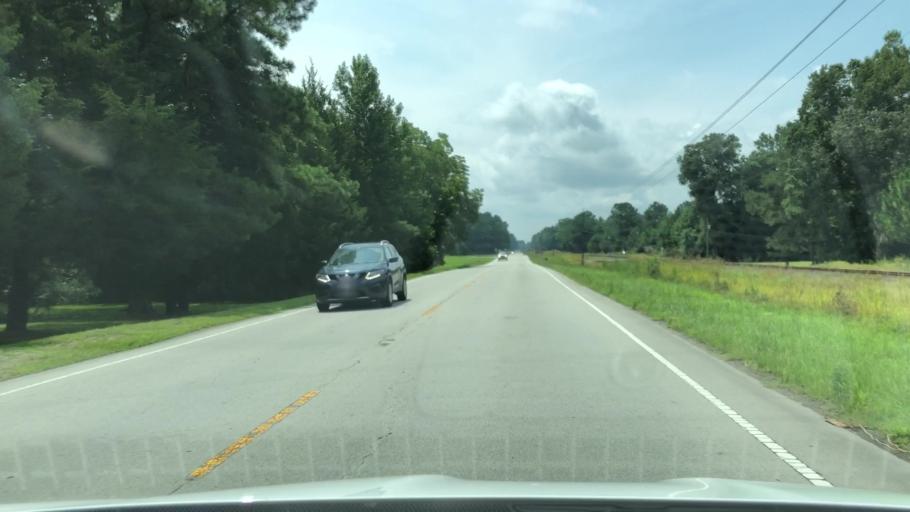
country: US
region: North Carolina
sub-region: Craven County
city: Vanceboro
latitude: 35.3449
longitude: -77.1510
